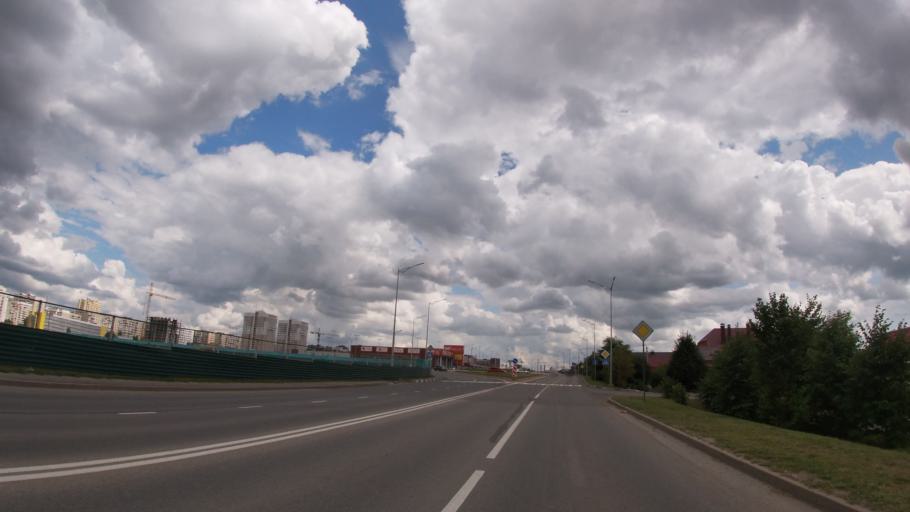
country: RU
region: Belgorod
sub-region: Belgorodskiy Rayon
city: Belgorod
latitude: 50.5509
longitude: 36.5606
